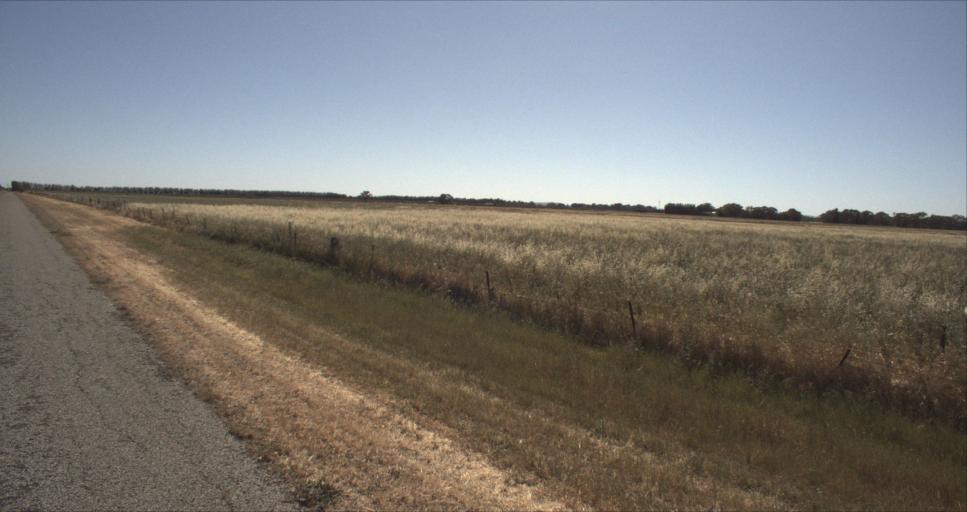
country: AU
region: New South Wales
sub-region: Leeton
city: Leeton
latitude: -34.5381
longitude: 146.3170
